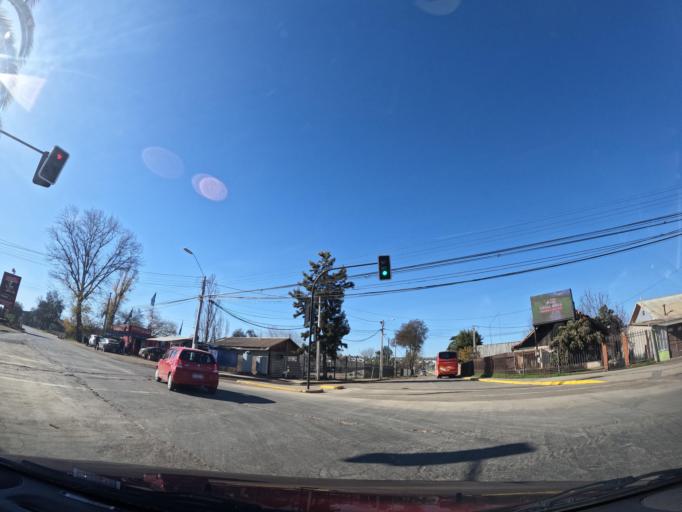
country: CL
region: Maule
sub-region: Provincia de Cauquenes
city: Cauquenes
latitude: -35.9615
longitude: -72.3125
